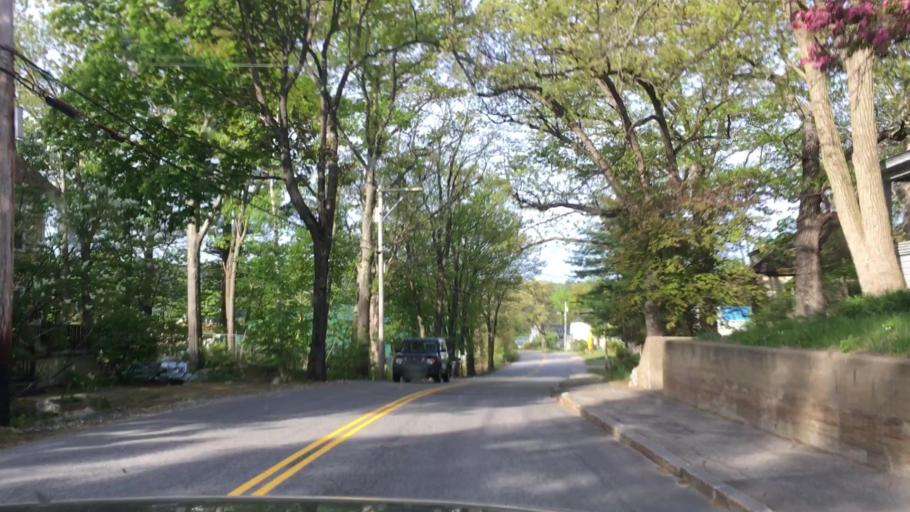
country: US
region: New Hampshire
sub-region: Belknap County
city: Meredith
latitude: 43.6512
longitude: -71.5031
